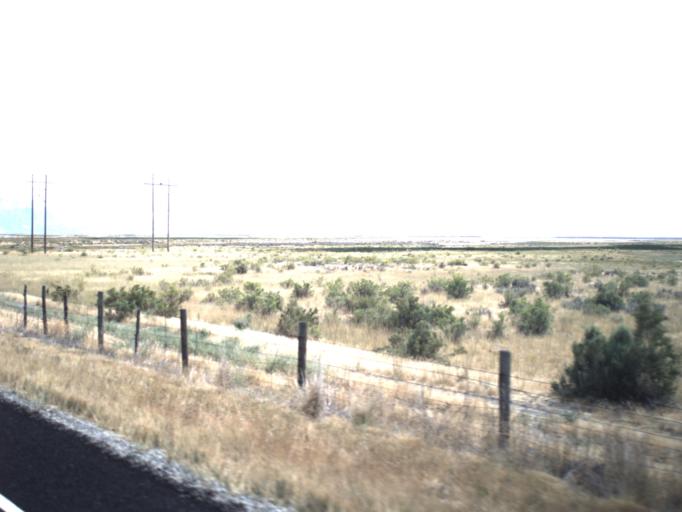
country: US
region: Utah
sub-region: Box Elder County
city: Tremonton
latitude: 41.6142
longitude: -112.3752
